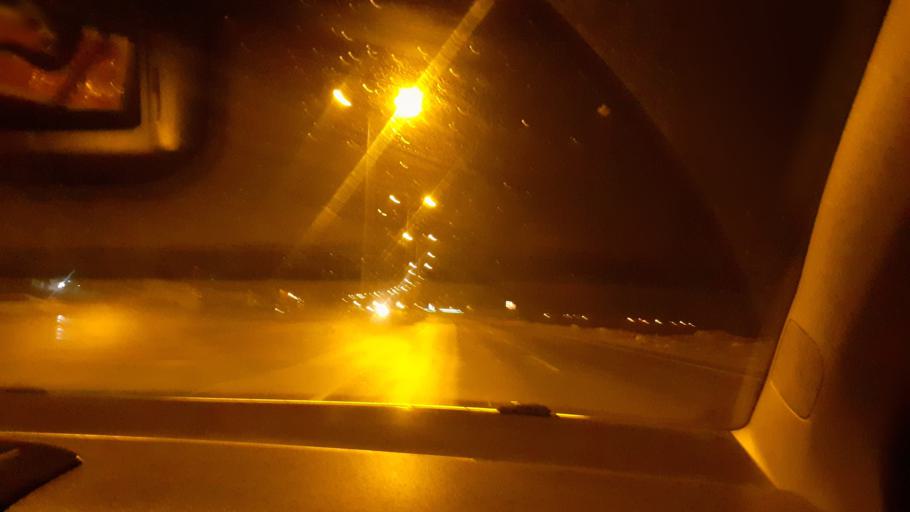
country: TR
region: Hatay
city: Aktepe
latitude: 36.7242
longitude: 36.5191
